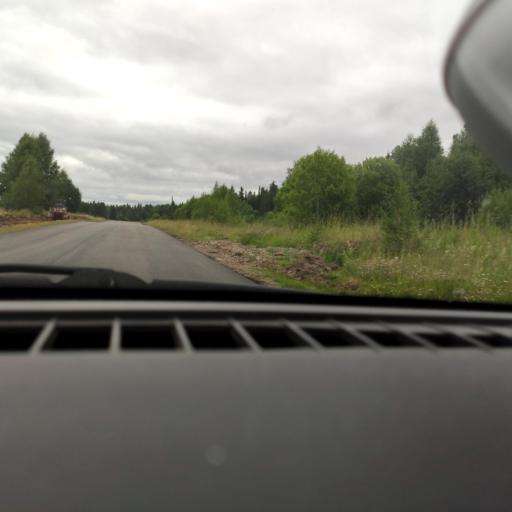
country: RU
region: Perm
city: Polazna
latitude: 58.3375
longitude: 56.2102
